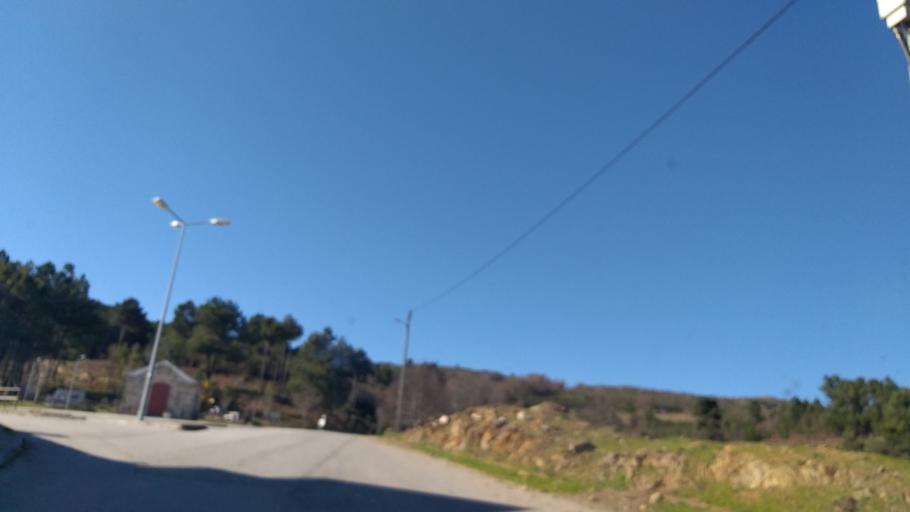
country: PT
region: Guarda
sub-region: Celorico da Beira
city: Celorico da Beira
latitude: 40.5210
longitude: -7.3926
